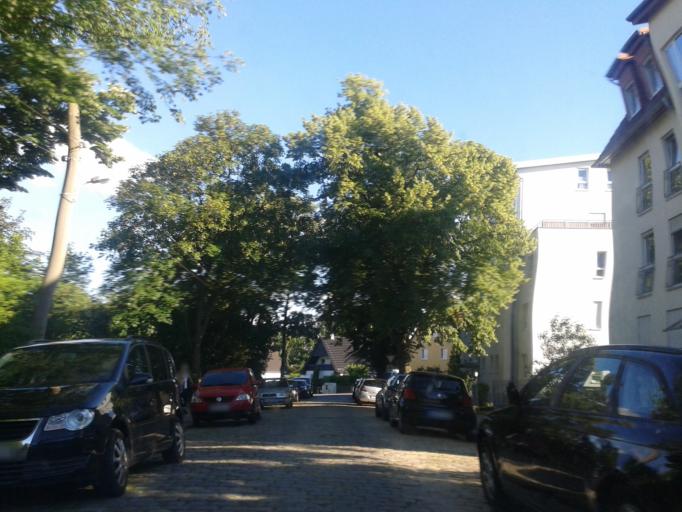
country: DE
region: Saxony
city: Radebeul
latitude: 51.0542
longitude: 13.6712
